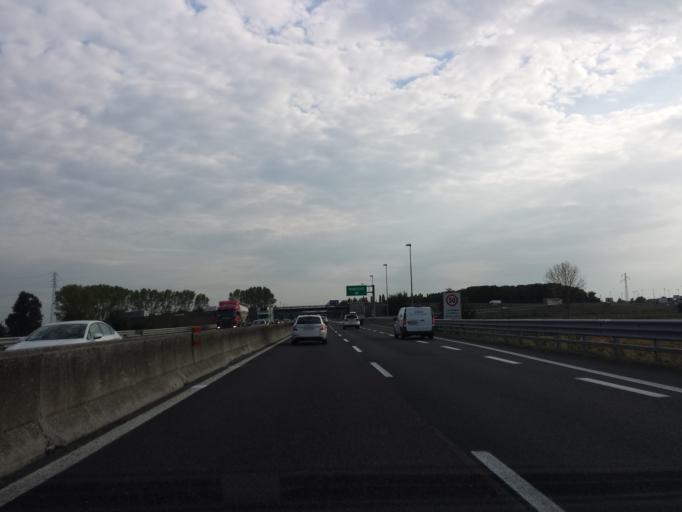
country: IT
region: Veneto
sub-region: Provincia di Padova
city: Pernumia
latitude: 45.2423
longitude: 11.7745
